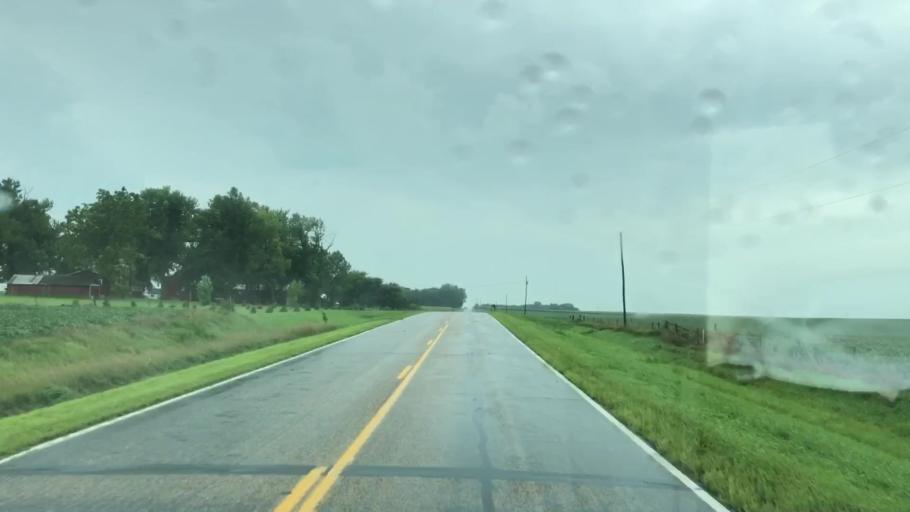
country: US
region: Iowa
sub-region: O'Brien County
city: Sanborn
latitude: 43.2728
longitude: -95.7127
